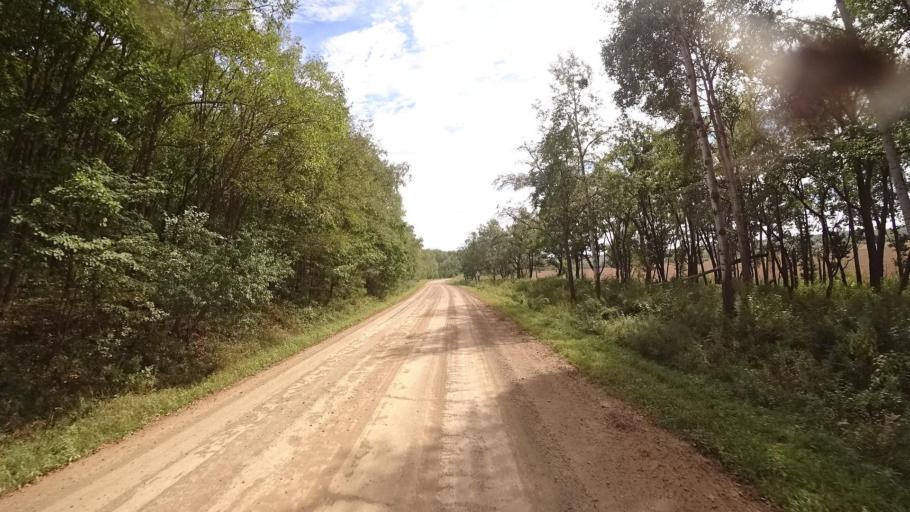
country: RU
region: Primorskiy
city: Yakovlevka
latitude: 44.5712
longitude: 133.5933
